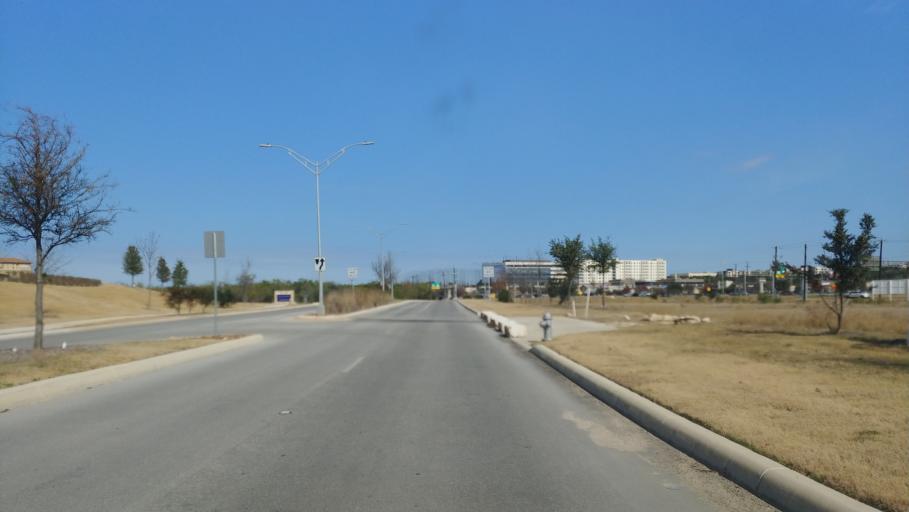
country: US
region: Texas
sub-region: Bexar County
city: Shavano Park
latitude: 29.5821
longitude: -98.5993
